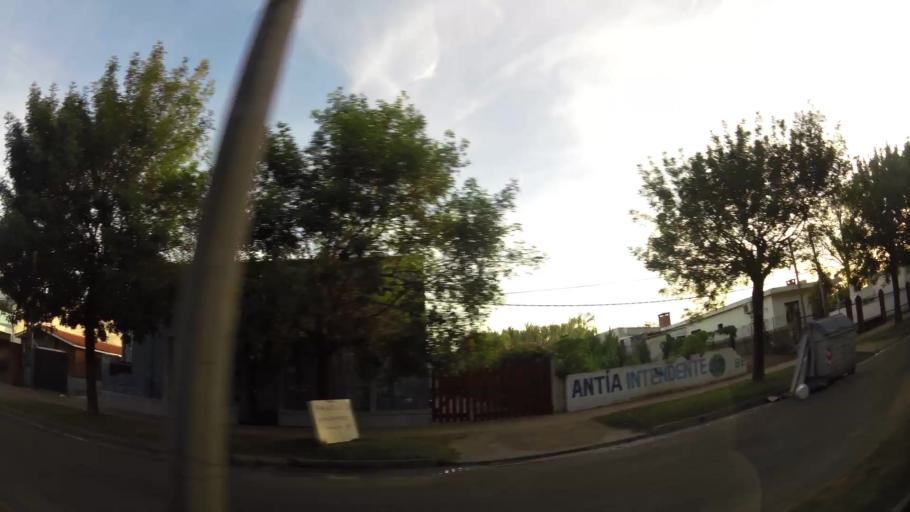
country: UY
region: Maldonado
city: Maldonado
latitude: -34.9082
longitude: -54.9504
